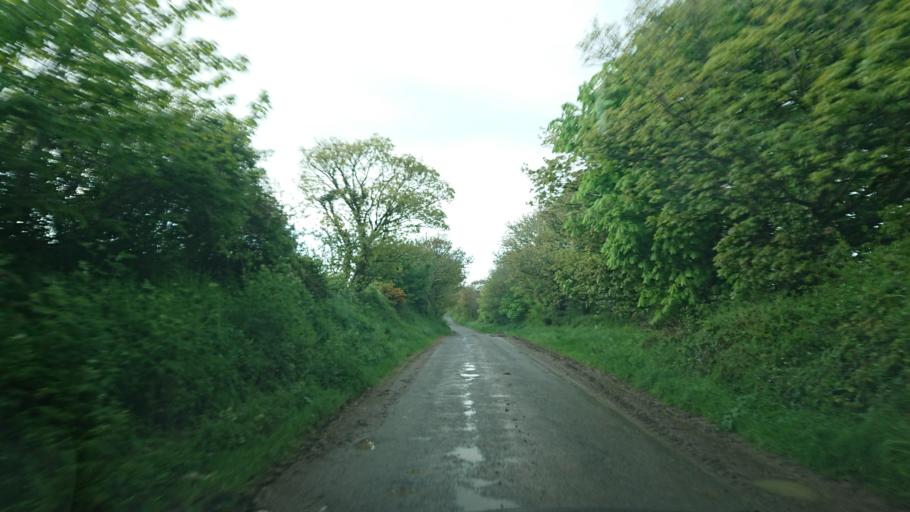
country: IE
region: Munster
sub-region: Waterford
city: Waterford
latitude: 52.2304
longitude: -7.1295
